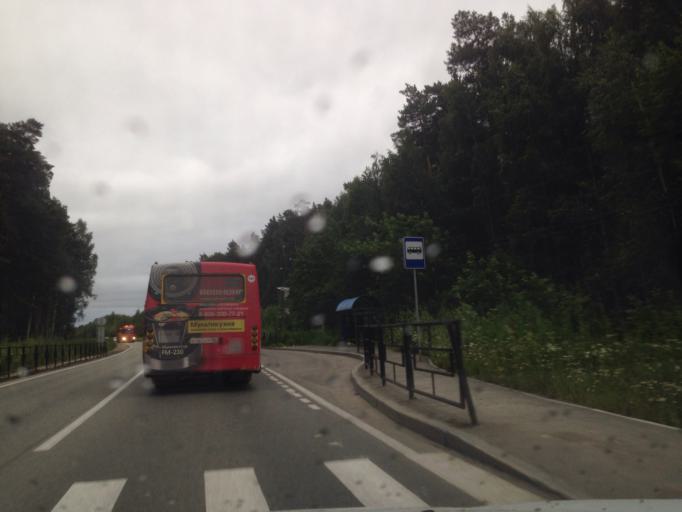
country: RU
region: Sverdlovsk
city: Istok
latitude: 56.8445
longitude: 60.7242
